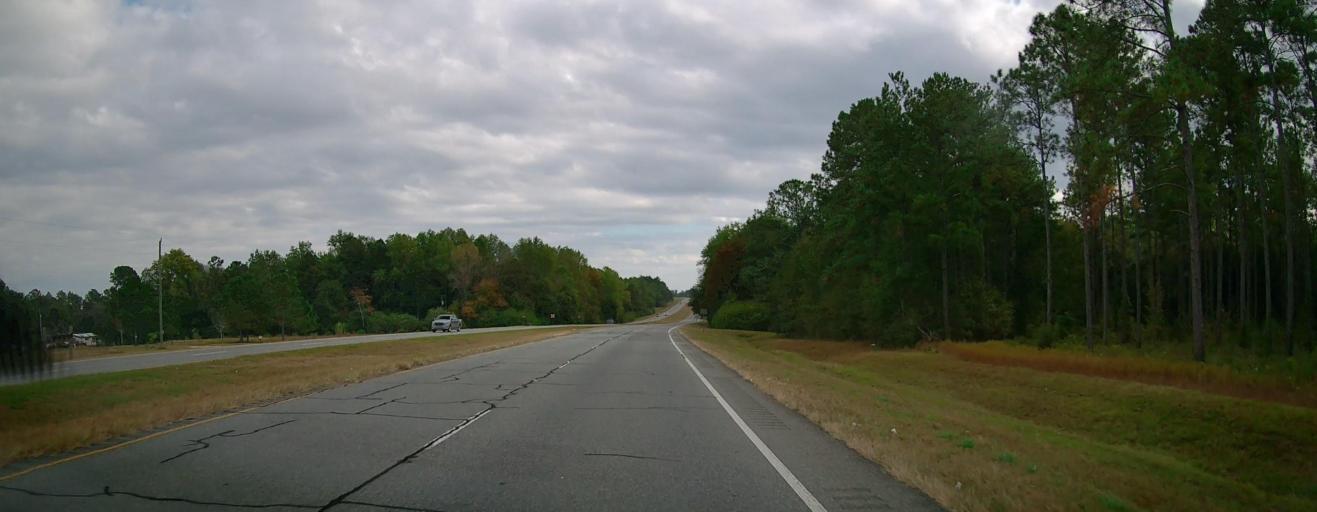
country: US
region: Georgia
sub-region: Thomas County
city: Meigs
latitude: 31.0967
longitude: -84.0968
